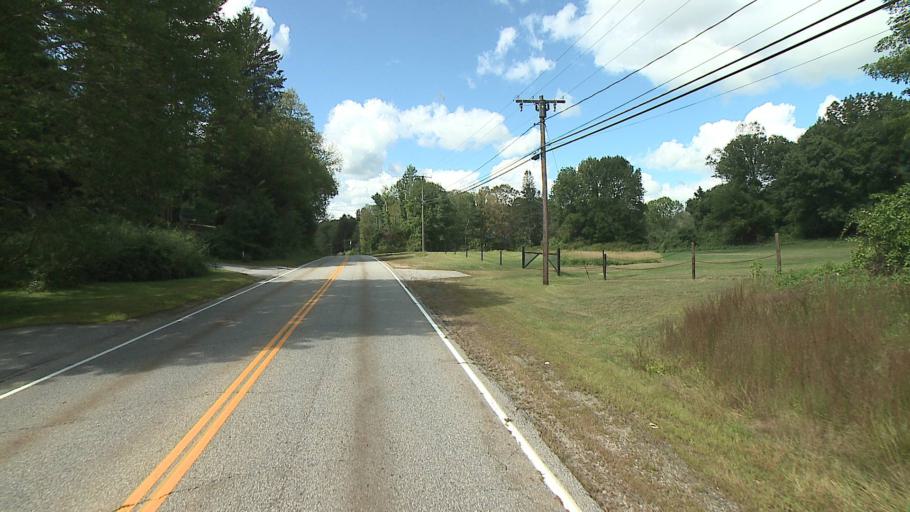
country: US
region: Connecticut
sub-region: Windham County
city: South Woodstock
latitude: 41.8615
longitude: -71.9795
